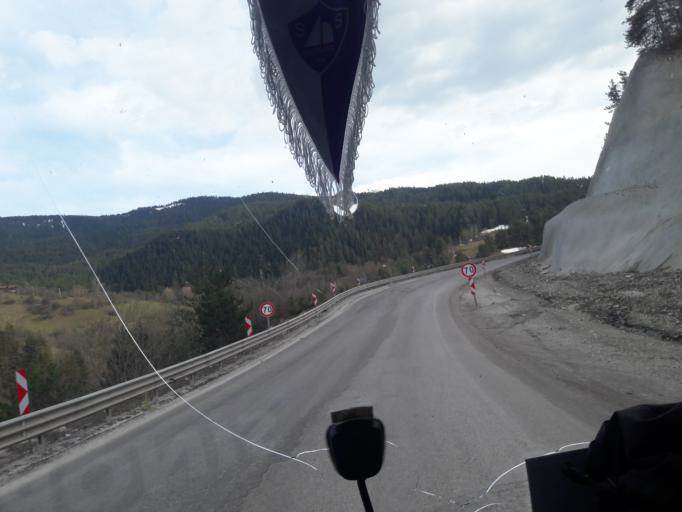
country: TR
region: Kastamonu
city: Kuzyaka
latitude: 41.1086
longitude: 33.7514
